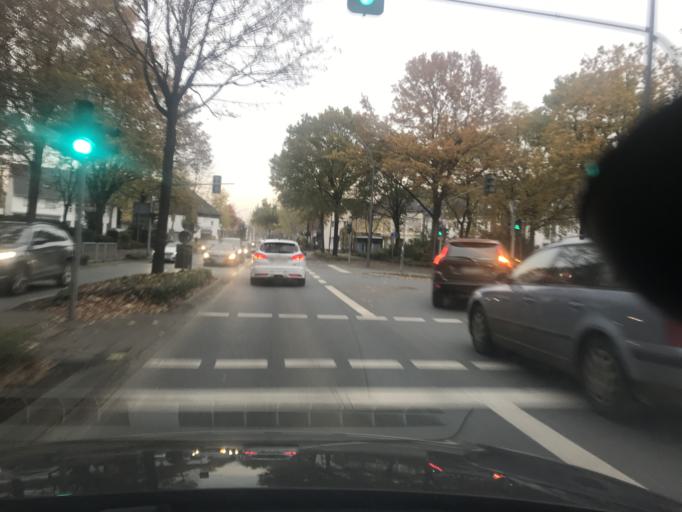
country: DE
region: North Rhine-Westphalia
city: Oelde
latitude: 51.8208
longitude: 8.1445
